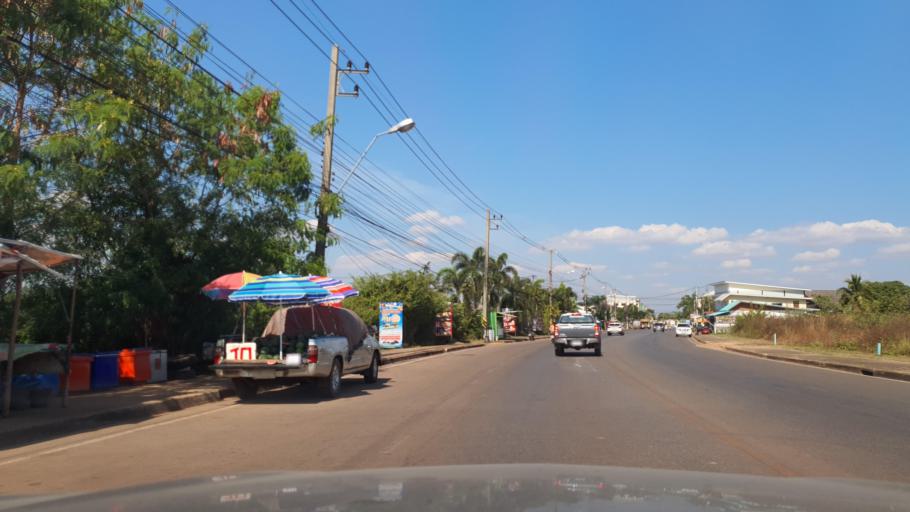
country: TH
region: Sakon Nakhon
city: Sakon Nakhon
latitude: 17.1708
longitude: 104.1258
